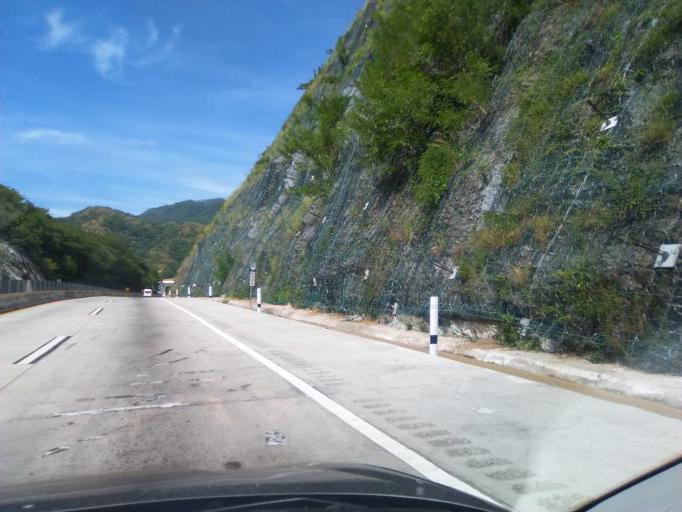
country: MX
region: Guerrero
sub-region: Acapulco de Juarez
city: Pueblo Madero (El Playon)
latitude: 17.0856
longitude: -99.5974
